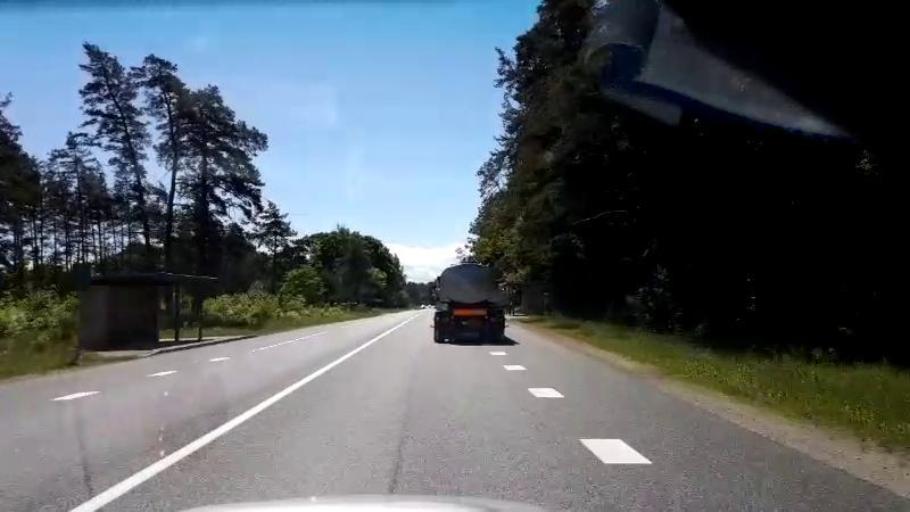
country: LV
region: Saulkrastu
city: Saulkrasti
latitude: 57.3890
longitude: 24.4288
